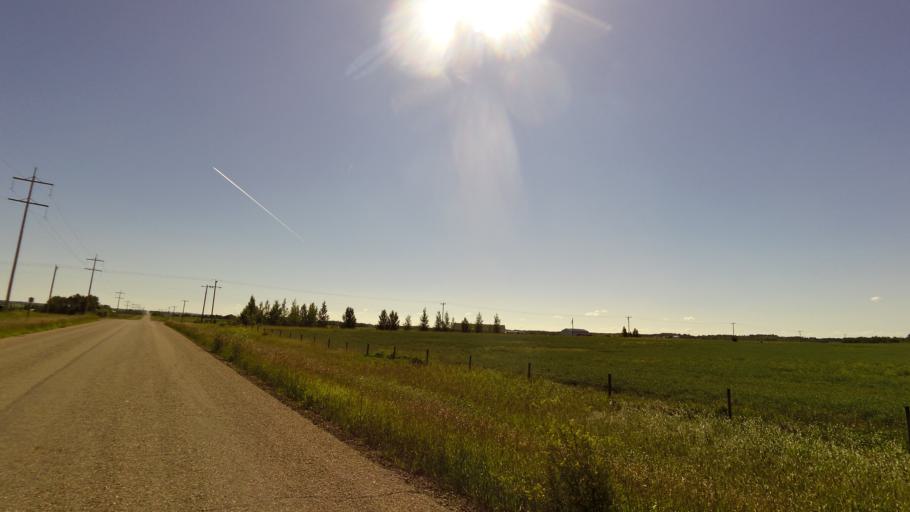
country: CA
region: Alberta
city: Wainwright
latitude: 52.8725
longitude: -110.9973
